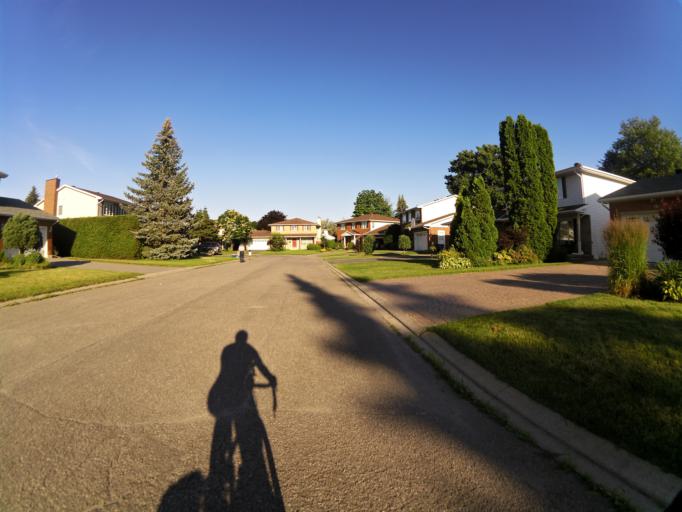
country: CA
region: Ontario
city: Bells Corners
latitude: 45.3332
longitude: -75.7726
